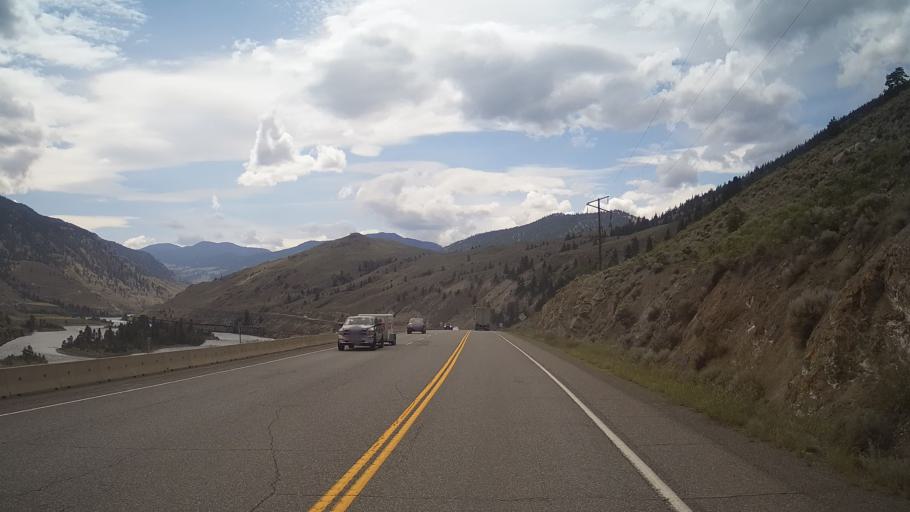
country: CA
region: British Columbia
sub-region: Thompson-Nicola Regional District
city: Ashcroft
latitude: 50.4893
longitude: -121.2981
